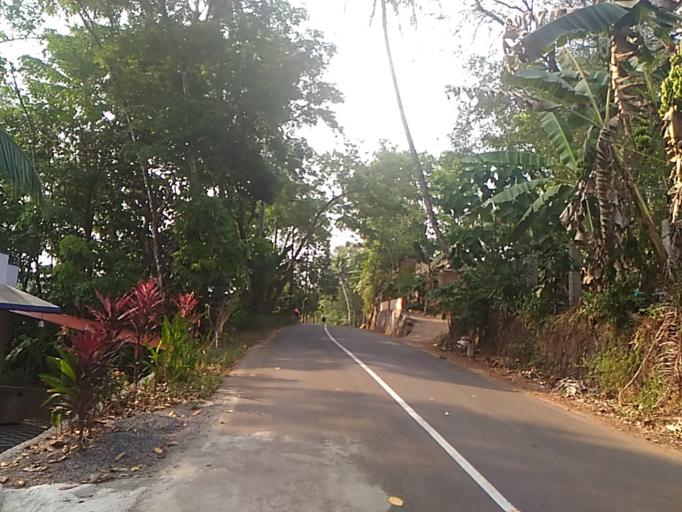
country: IN
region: Kerala
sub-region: Kottayam
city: Palackattumala
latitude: 9.7820
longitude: 76.6723
